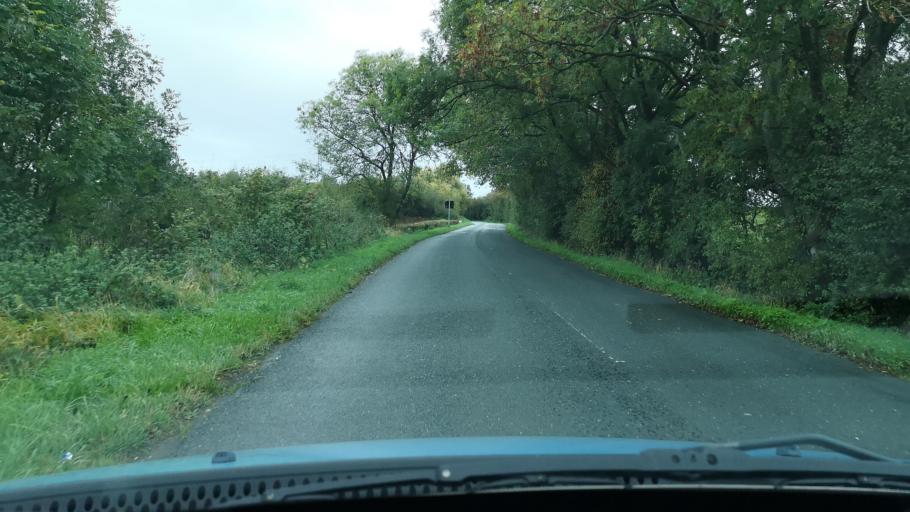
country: GB
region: England
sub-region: Doncaster
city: Hatfield
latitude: 53.6220
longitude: -0.9837
